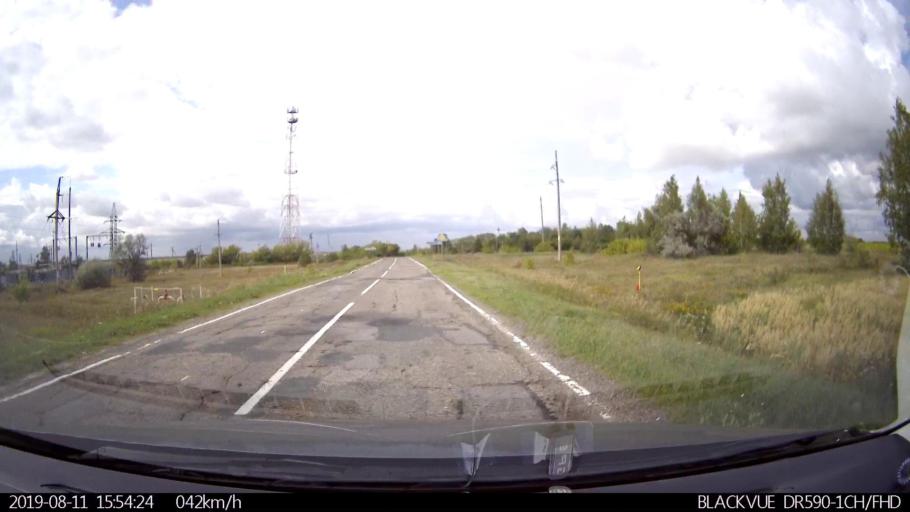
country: RU
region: Ulyanovsk
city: Ignatovka
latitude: 53.9409
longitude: 47.6565
